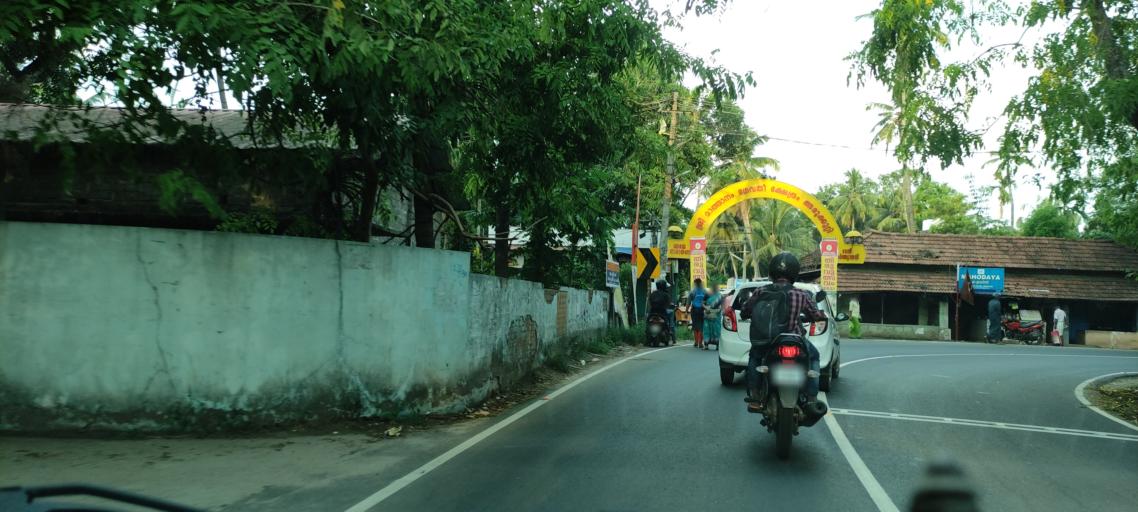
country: IN
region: Kerala
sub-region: Alappuzha
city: Arukutti
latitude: 9.8701
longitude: 76.3241
